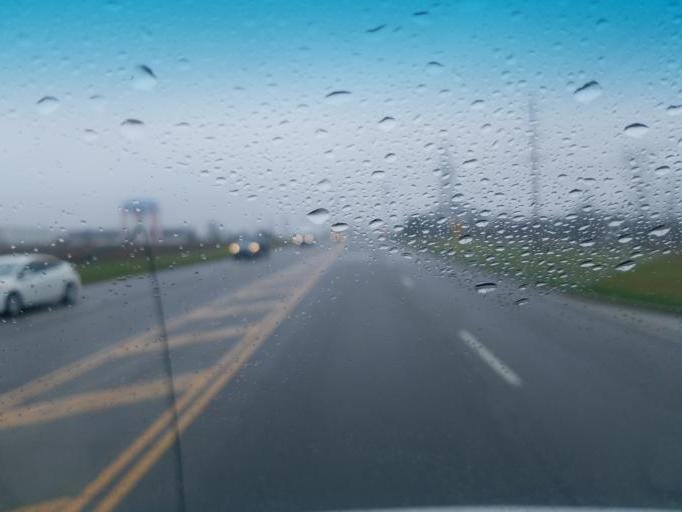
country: US
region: Ohio
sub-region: Hancock County
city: Findlay
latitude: 41.0878
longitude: -83.6478
